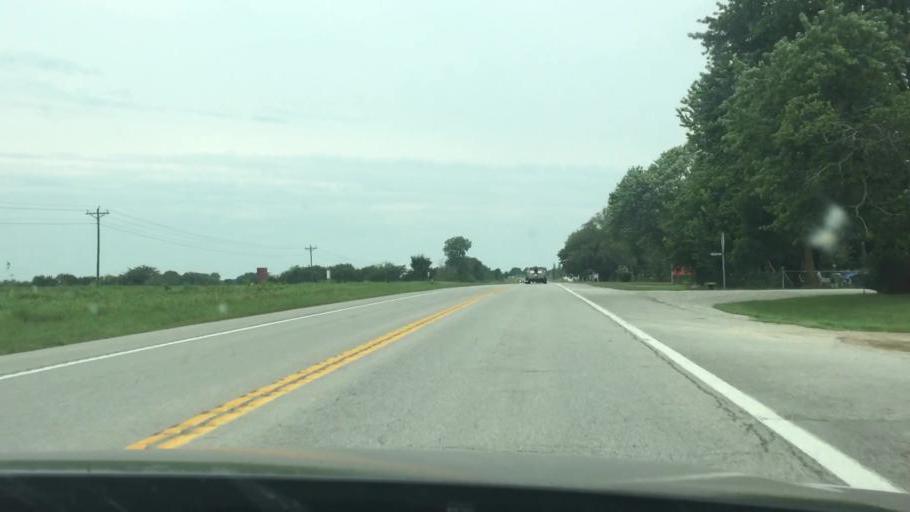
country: US
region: Missouri
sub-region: Pettis County
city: Sedalia
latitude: 38.6955
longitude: -93.1586
